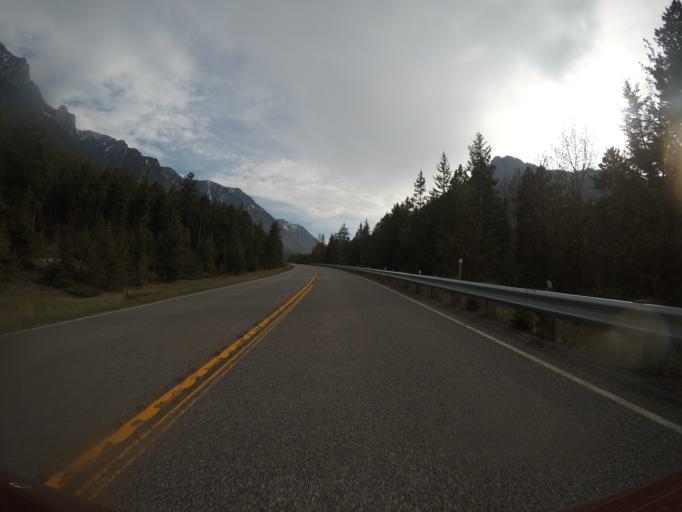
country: US
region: Montana
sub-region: Carbon County
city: Red Lodge
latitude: 45.0764
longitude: -109.3830
